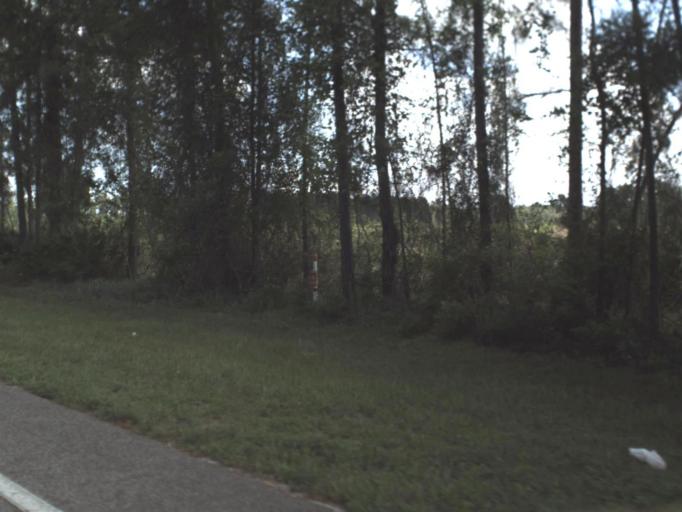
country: US
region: Florida
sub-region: Putnam County
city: East Palatka
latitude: 29.5781
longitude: -81.5560
